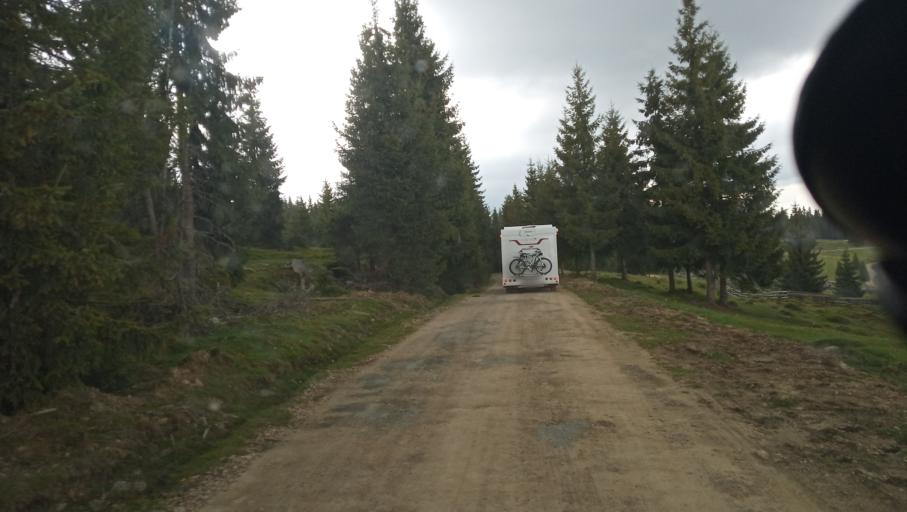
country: RO
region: Cluj
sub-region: Comuna Belis
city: Belis
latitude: 46.6316
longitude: 23.0441
